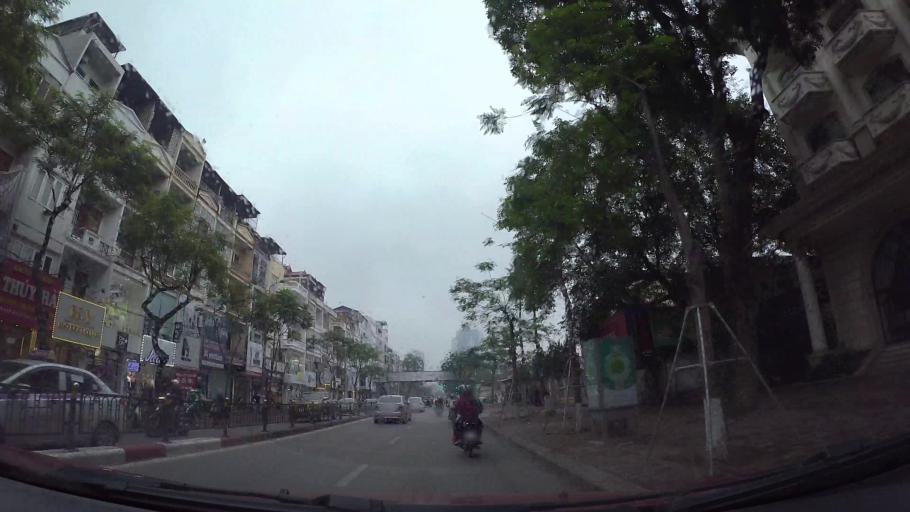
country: VN
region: Ha Noi
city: Dong Da
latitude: 21.0073
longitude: 105.8291
